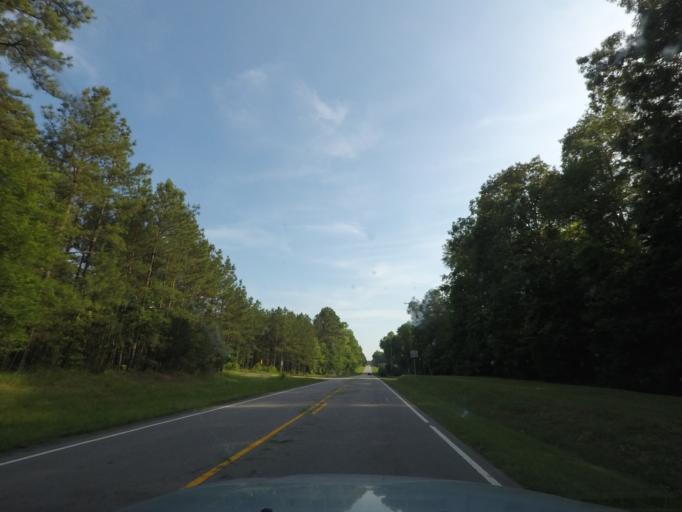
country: US
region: Virginia
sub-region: Mecklenburg County
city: Clarksville
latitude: 36.4685
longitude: -78.5580
